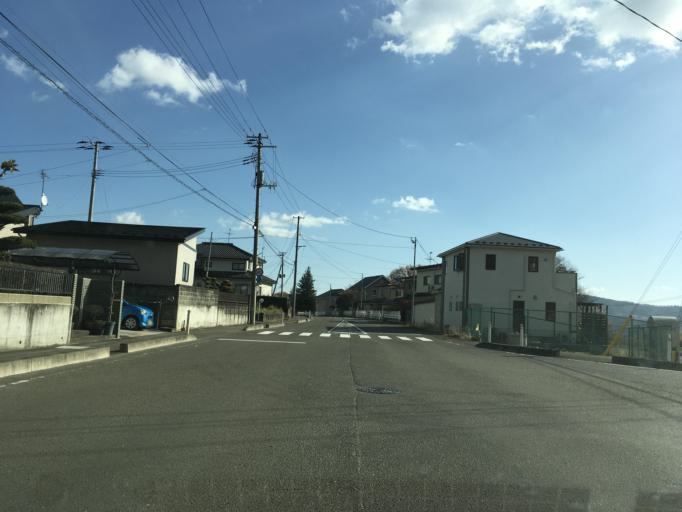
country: JP
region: Miyagi
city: Sendai
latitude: 38.2868
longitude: 140.7514
